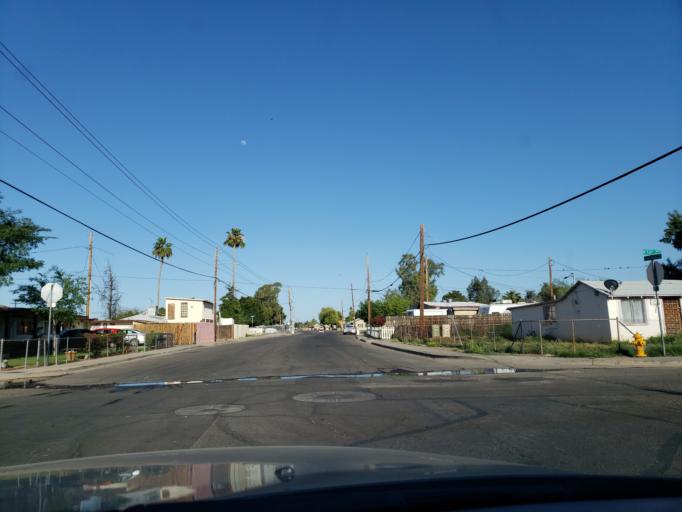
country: US
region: Arizona
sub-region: Maricopa County
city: Glendale
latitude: 33.5349
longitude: -112.1738
